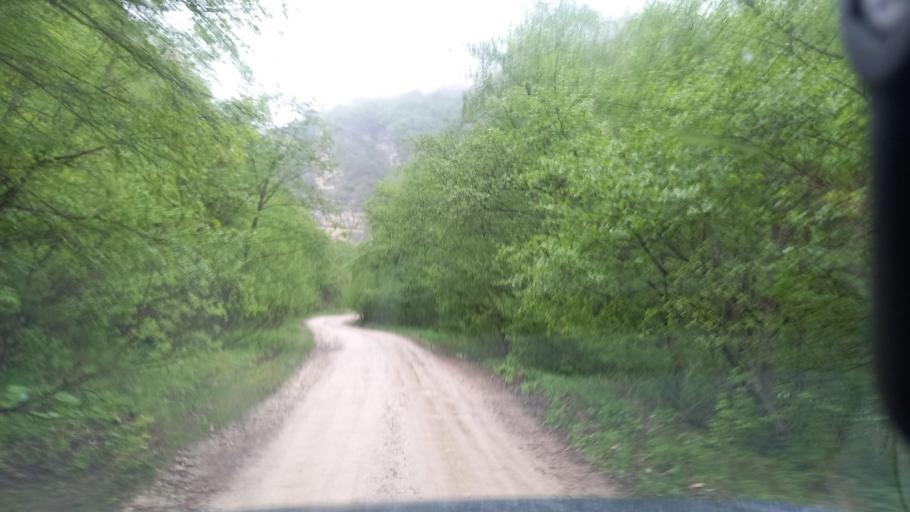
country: RU
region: Kabardino-Balkariya
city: Gundelen
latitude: 43.5828
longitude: 43.1175
